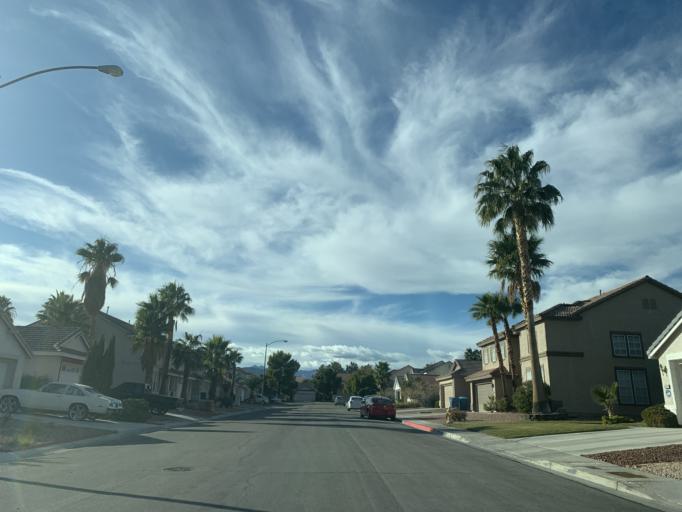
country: US
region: Nevada
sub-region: Clark County
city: Summerlin South
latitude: 36.1266
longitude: -115.3007
